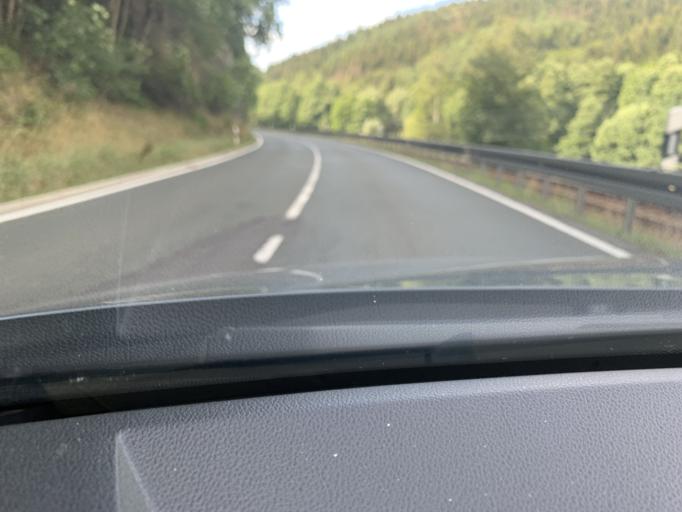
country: DE
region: Thuringia
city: Judenbach
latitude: 50.4062
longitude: 11.1870
